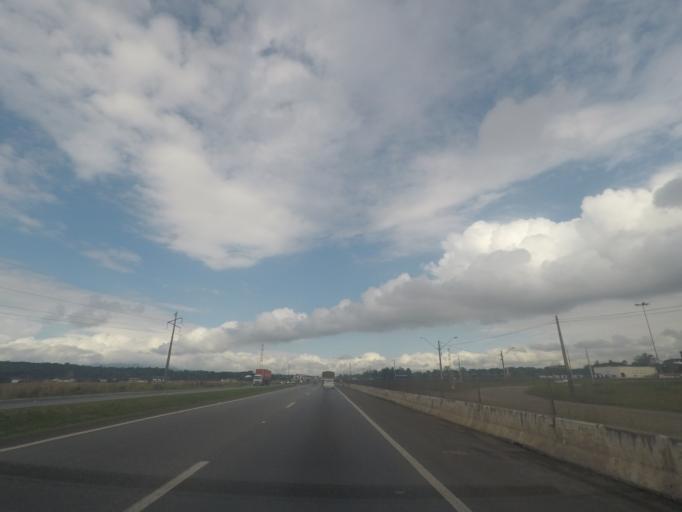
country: BR
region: Parana
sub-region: Piraquara
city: Piraquara
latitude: -25.5190
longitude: -49.1116
